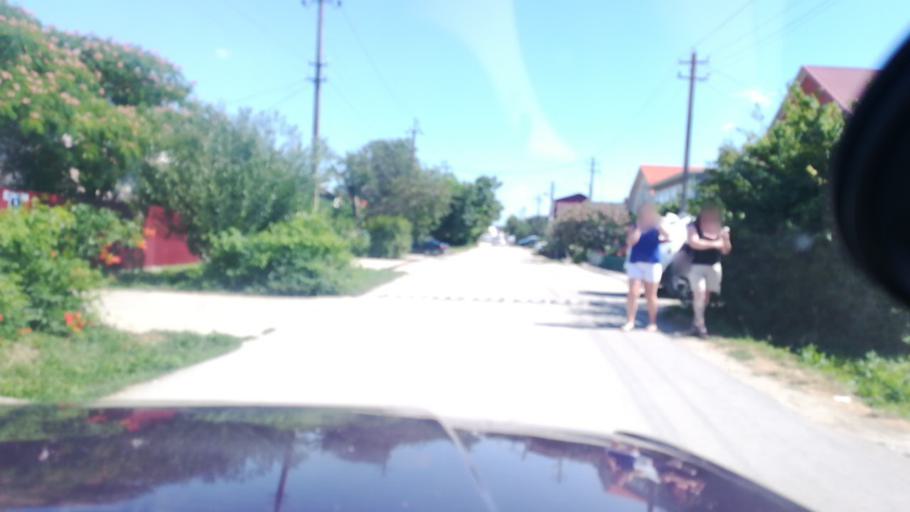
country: RU
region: Krasnodarskiy
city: Vityazevo
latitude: 44.9937
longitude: 37.2736
